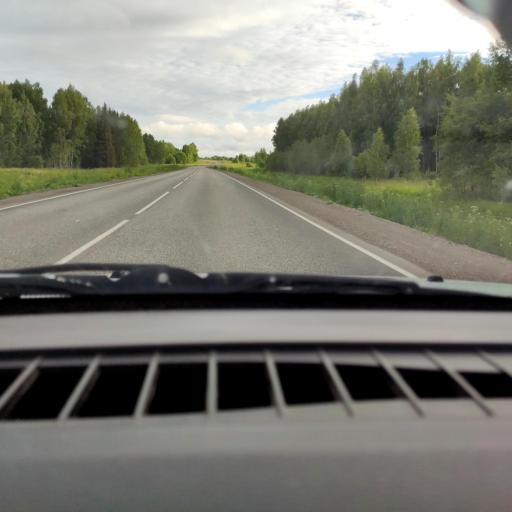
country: RU
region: Perm
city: Kungur
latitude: 57.3377
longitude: 56.9670
